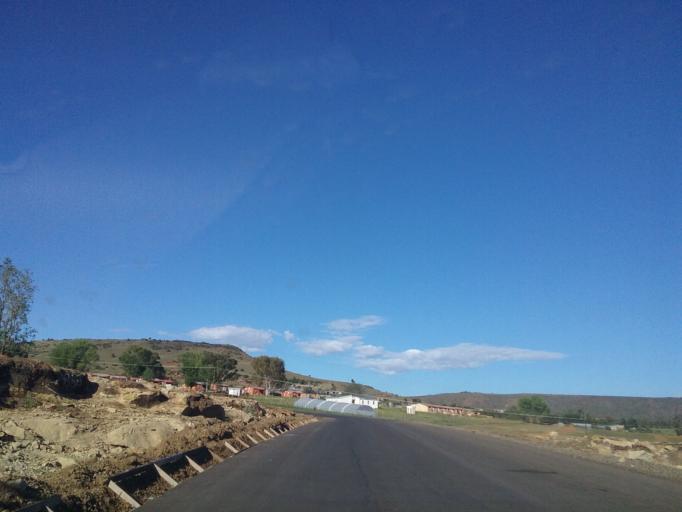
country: LS
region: Quthing
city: Quthing
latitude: -30.4049
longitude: 27.7022
